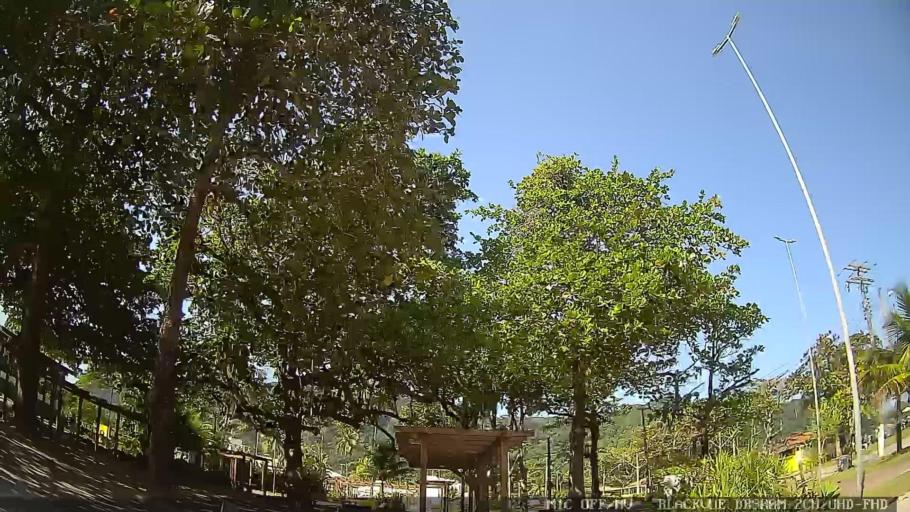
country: BR
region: Sao Paulo
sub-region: Guaruja
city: Guaruja
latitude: -24.0194
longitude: -46.2976
